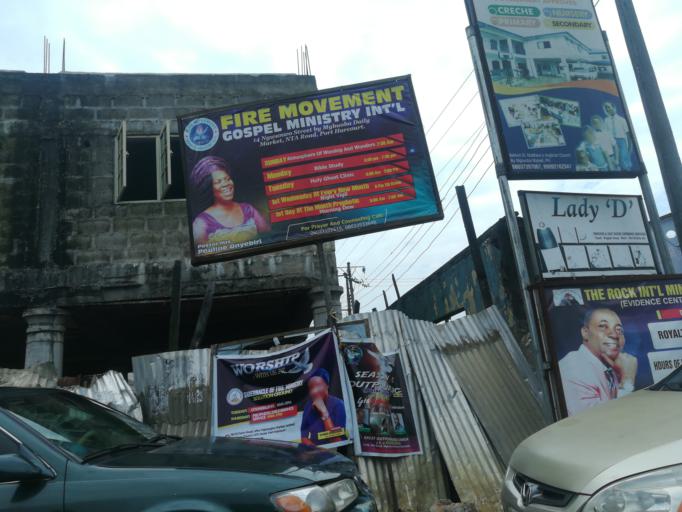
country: NG
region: Rivers
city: Port Harcourt
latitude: 4.8482
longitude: 6.9789
